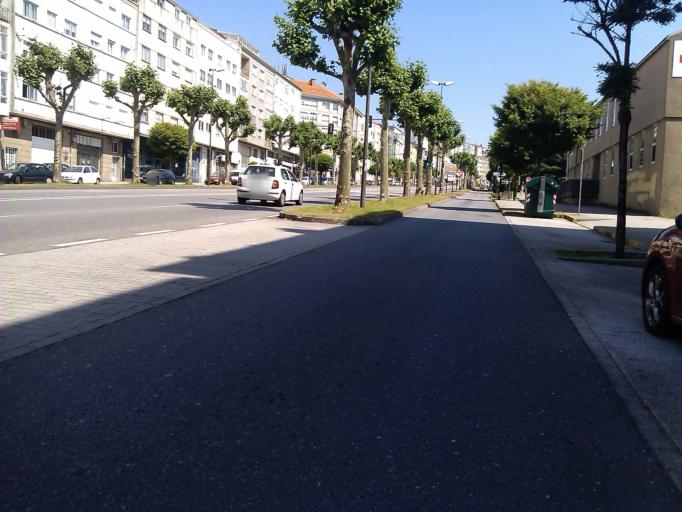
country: ES
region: Galicia
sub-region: Provincia da Coruna
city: Santiago de Compostela
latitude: 42.8815
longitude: -8.5330
